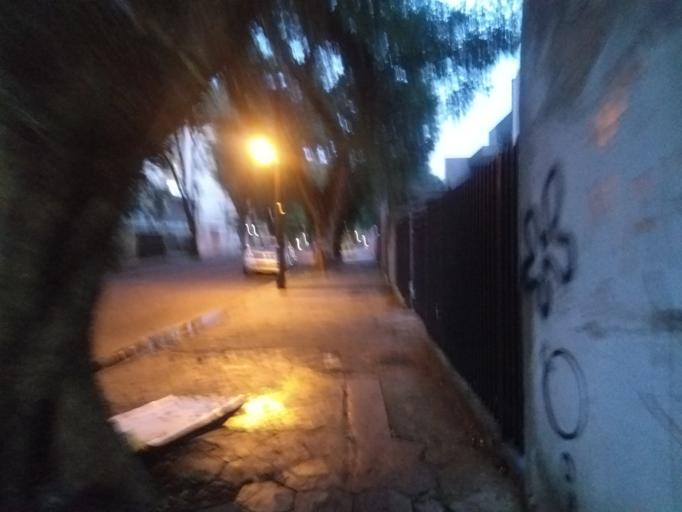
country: BR
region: Parana
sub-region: Maringa
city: Maringa
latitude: -23.4151
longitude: -51.9327
